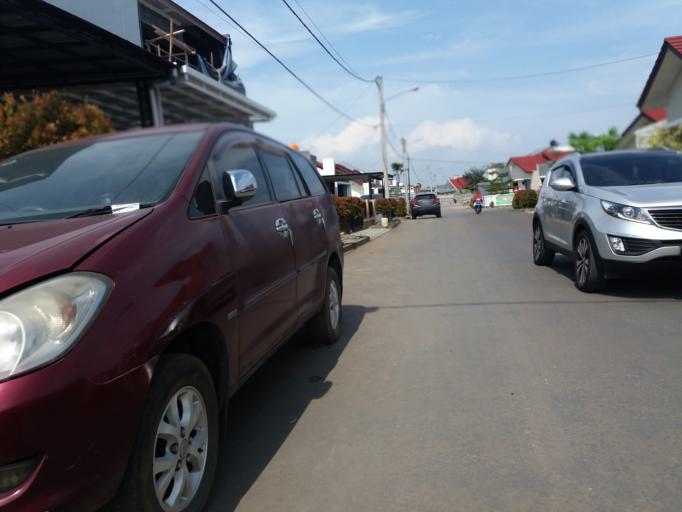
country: ID
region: West Java
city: Bandung
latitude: -6.9235
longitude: 107.6681
